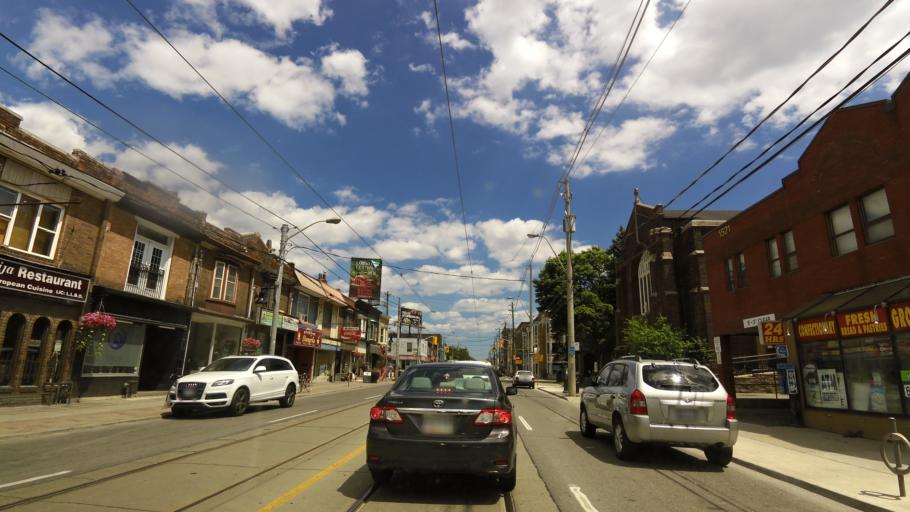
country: CA
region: Ontario
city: Toronto
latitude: 43.6395
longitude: -79.4419
